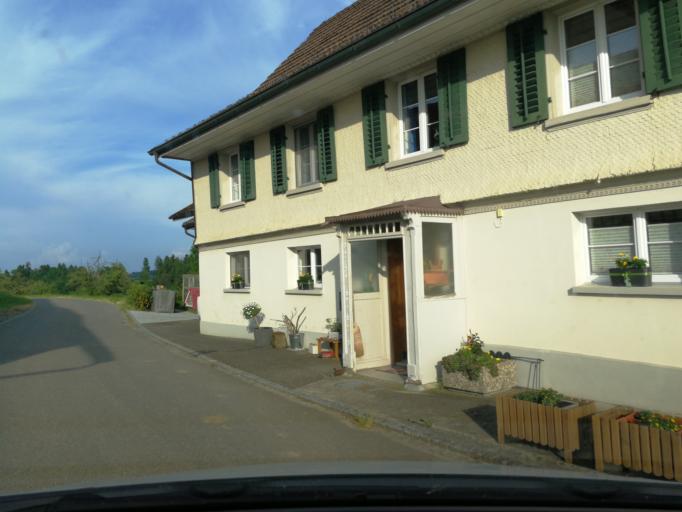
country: CH
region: Thurgau
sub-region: Weinfelden District
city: Sulgen
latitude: 47.5111
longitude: 9.1869
